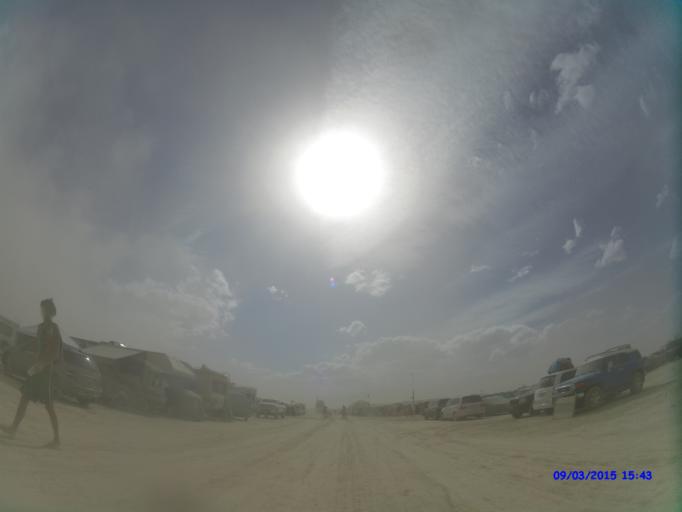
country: US
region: Nevada
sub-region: Pershing County
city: Lovelock
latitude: 40.7948
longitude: -119.2122
